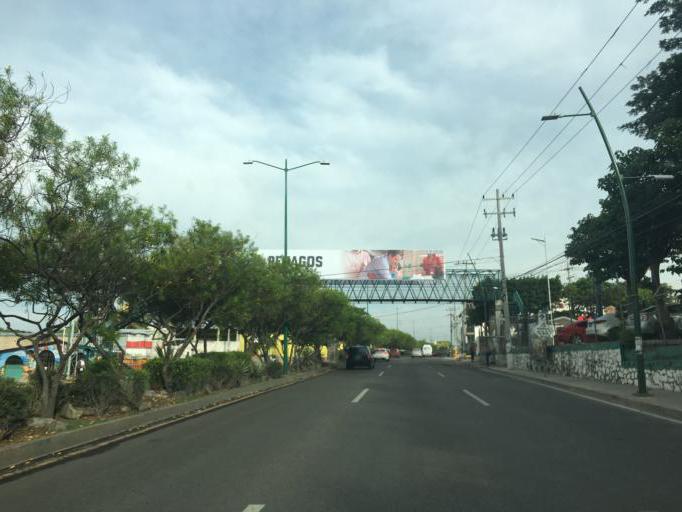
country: MX
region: Chiapas
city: Tuxtla Gutierrez
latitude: 16.7610
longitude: -93.1484
